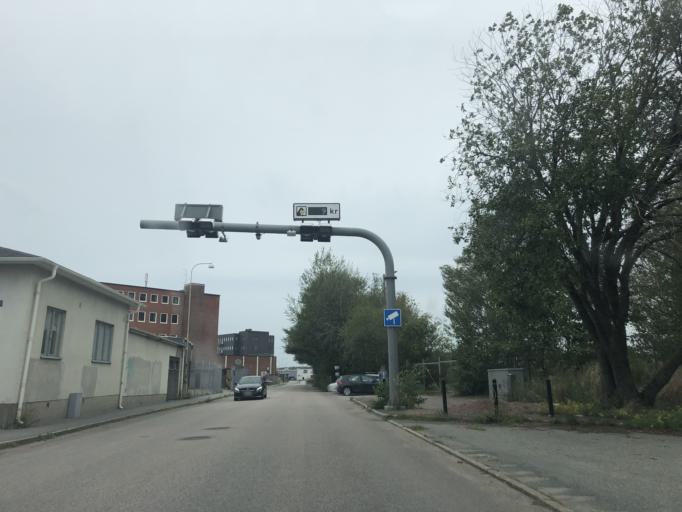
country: SE
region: Vaestra Goetaland
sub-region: Goteborg
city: Majorna
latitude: 57.7106
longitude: 11.9370
